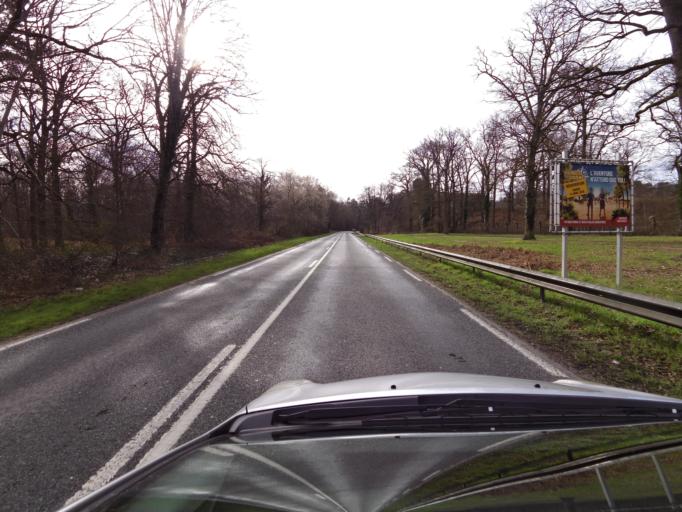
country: FR
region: Picardie
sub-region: Departement de l'Oise
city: Ver-sur-Launette
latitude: 49.1449
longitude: 2.6808
